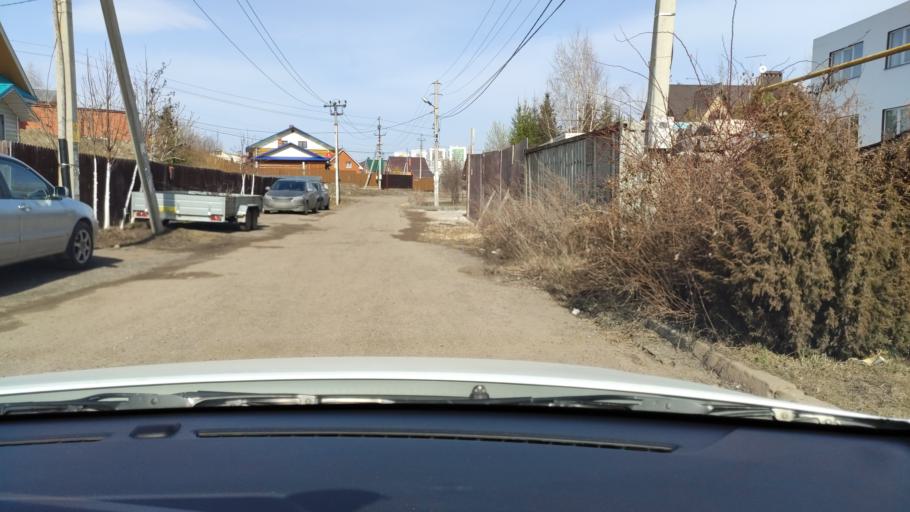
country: RU
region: Tatarstan
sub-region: Gorod Kazan'
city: Kazan
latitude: 55.7835
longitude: 49.2480
